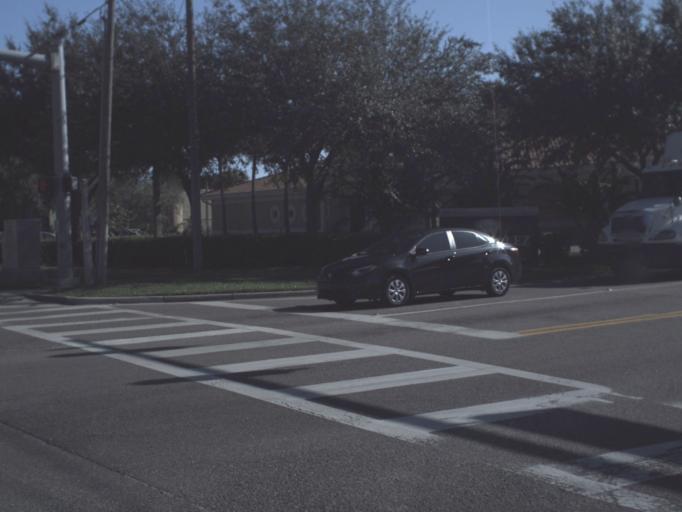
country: US
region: Florida
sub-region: Hillsborough County
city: Egypt Lake-Leto
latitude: 28.0144
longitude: -82.5049
